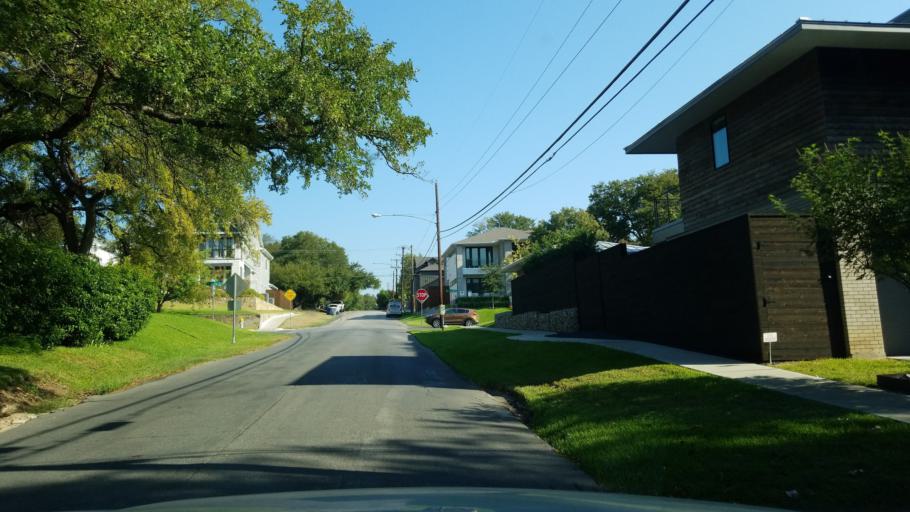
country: US
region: Texas
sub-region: Dallas County
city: Highland Park
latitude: 32.8104
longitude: -96.7388
